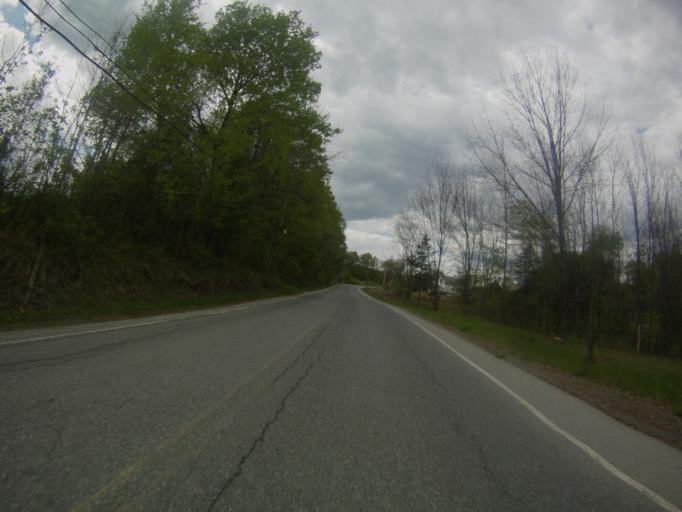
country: US
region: New York
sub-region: Essex County
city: Port Henry
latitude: 43.9507
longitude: -73.4775
